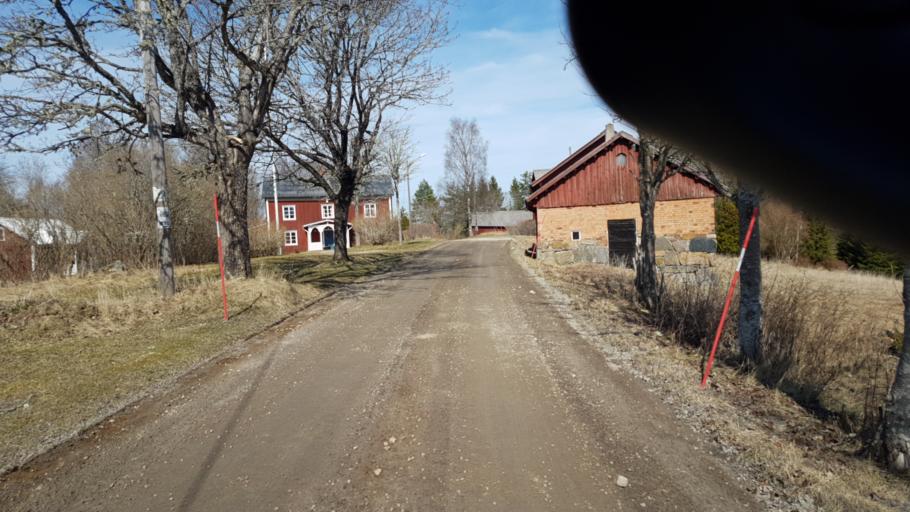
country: SE
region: Vaermland
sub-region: Arvika Kommun
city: Arvika
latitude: 59.5484
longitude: 12.8493
